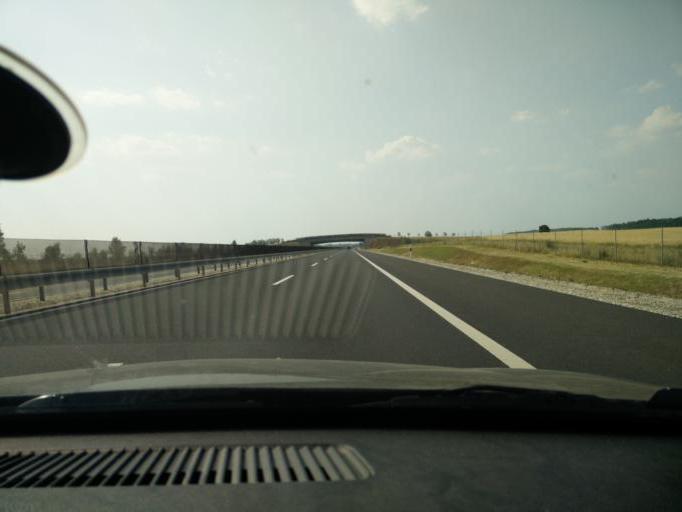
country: HU
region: Tolna
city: Szedres
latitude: 46.4290
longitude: 18.7195
